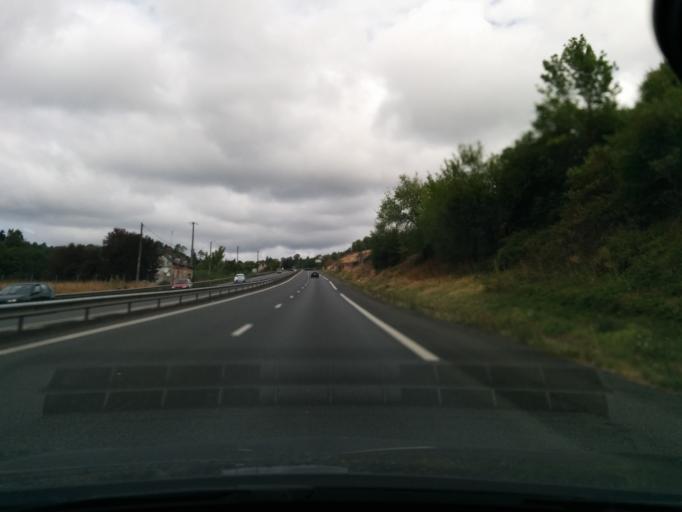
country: FR
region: Limousin
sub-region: Departement de la Correze
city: Brive-la-Gaillarde
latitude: 45.0927
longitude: 1.5197
